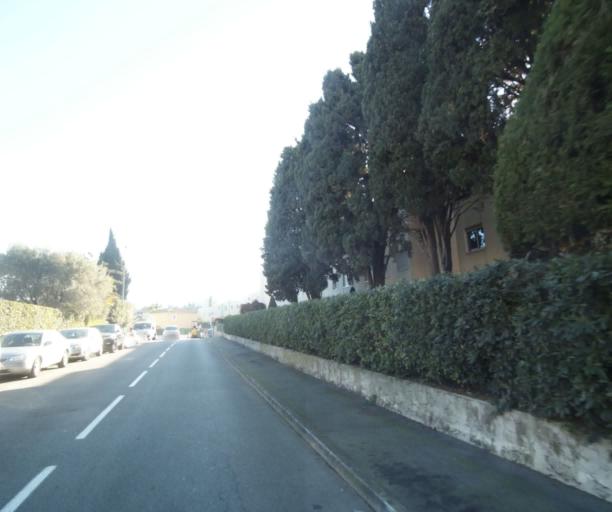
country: FR
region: Provence-Alpes-Cote d'Azur
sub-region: Departement des Alpes-Maritimes
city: Antibes
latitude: 43.5807
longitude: 7.0973
